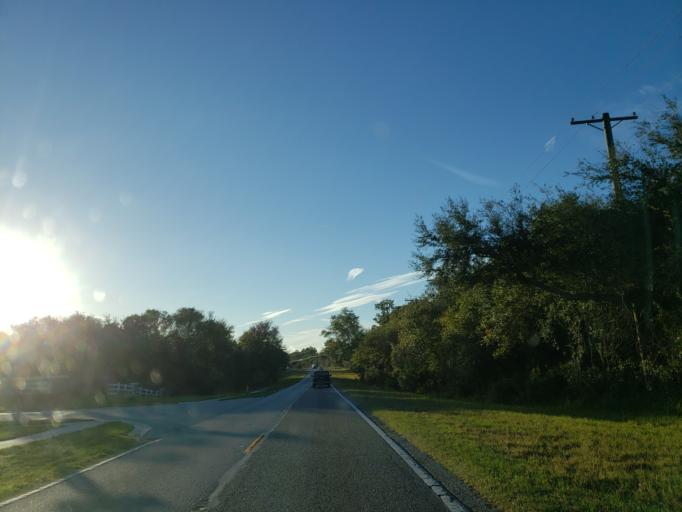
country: US
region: Florida
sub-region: Hillsborough County
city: Boyette
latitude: 27.8252
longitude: -82.2667
